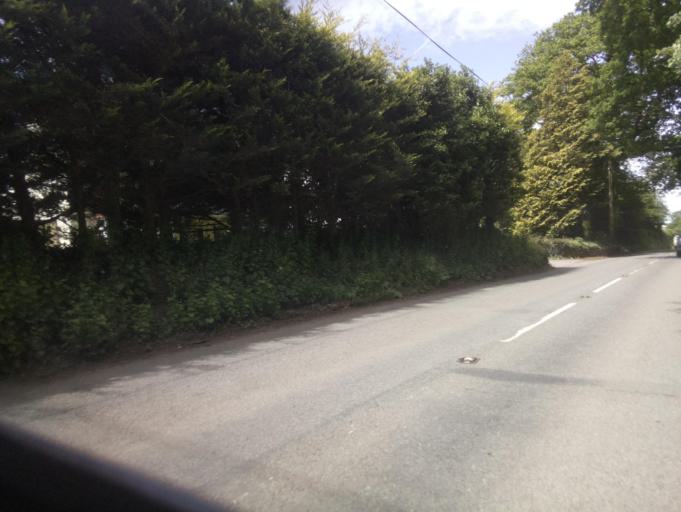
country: GB
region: England
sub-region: Devon
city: Ottery St Mary
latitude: 50.8263
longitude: -3.2958
